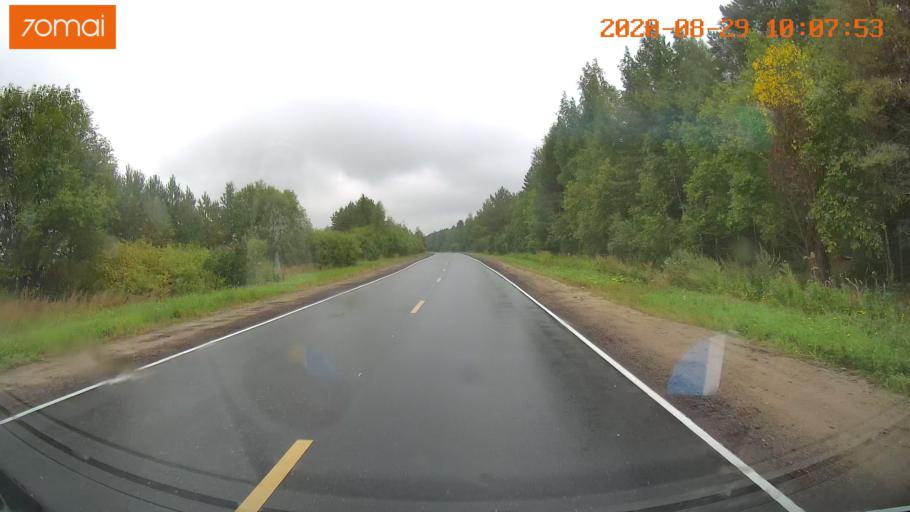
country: RU
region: Ivanovo
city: Kuznechikha
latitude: 57.3780
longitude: 42.5767
